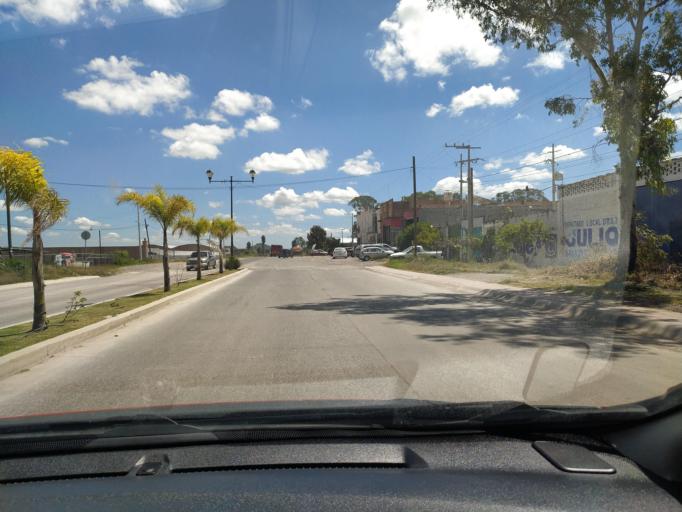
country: MX
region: Jalisco
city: San Julian
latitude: 21.0075
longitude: -102.1622
